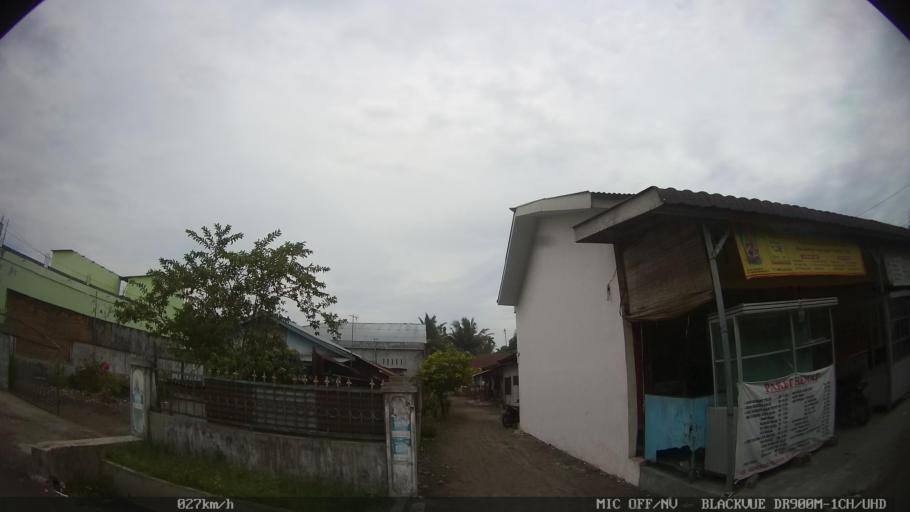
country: ID
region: North Sumatra
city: Binjai
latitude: 3.6300
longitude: 98.5553
